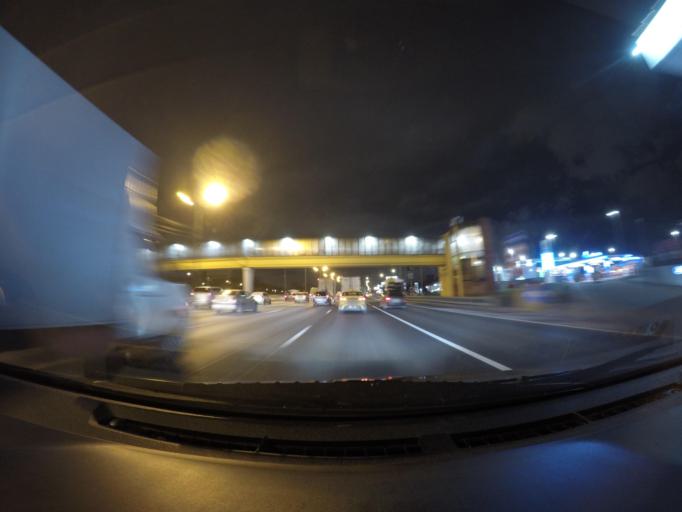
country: RU
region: Moskovskaya
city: Alekseyevka
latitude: 55.6264
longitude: 37.7986
